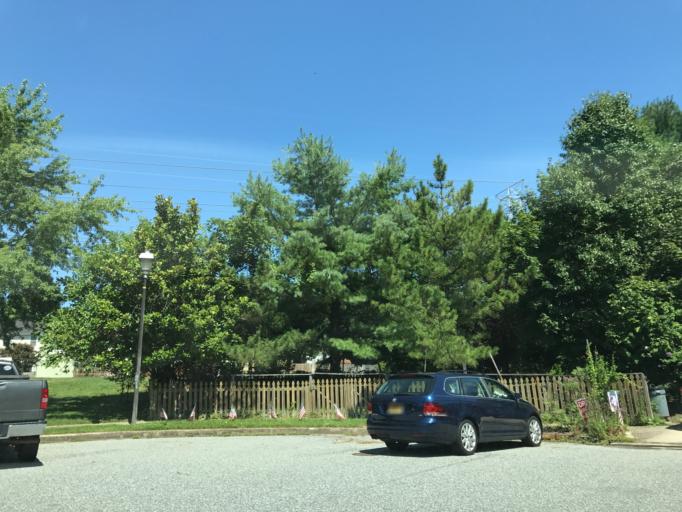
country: US
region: Maryland
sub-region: Baltimore County
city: Perry Hall
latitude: 39.3836
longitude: -76.4729
